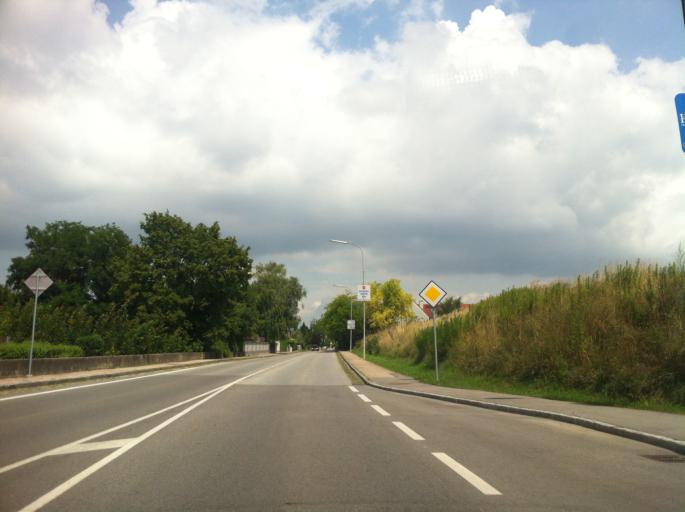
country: AT
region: Lower Austria
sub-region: Politischer Bezirk Tulln
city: Tulln
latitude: 48.3190
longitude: 16.0573
